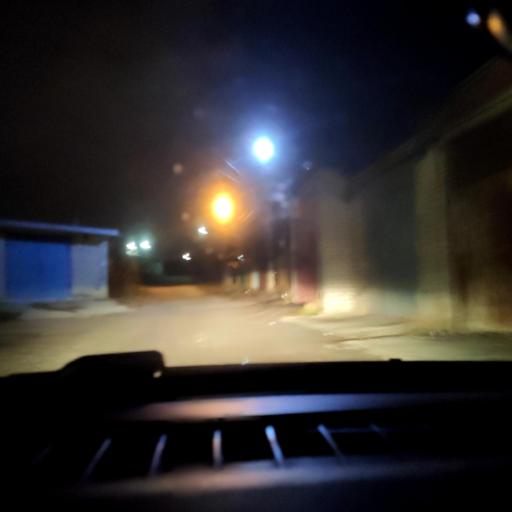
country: RU
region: Voronezj
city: Voronezh
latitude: 51.6386
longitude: 39.1287
